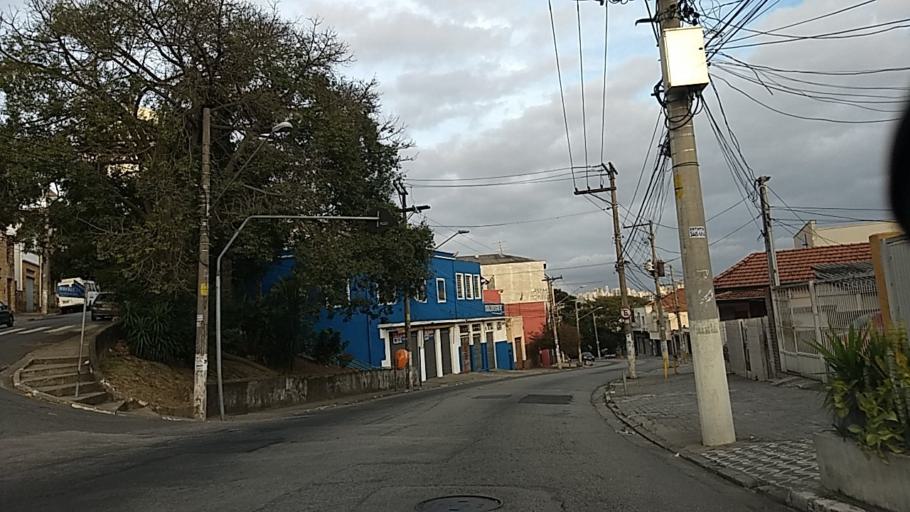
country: BR
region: Sao Paulo
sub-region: Sao Paulo
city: Sao Paulo
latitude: -23.5104
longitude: -46.5871
